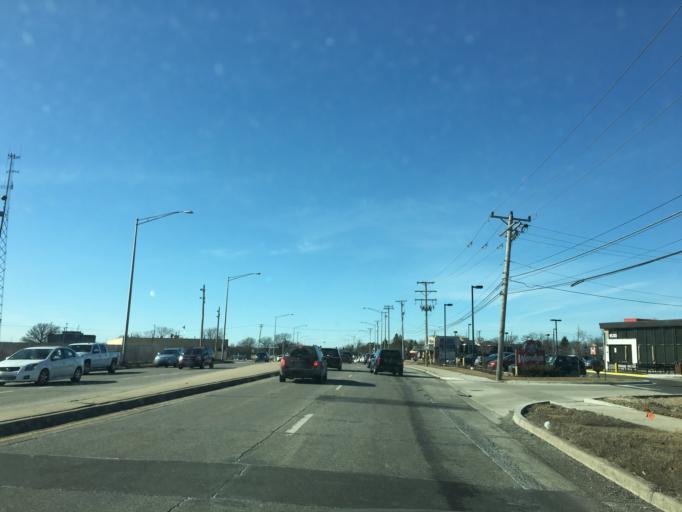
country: US
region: Illinois
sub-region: Cook County
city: Rolling Meadows
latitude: 42.0673
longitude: -88.0406
